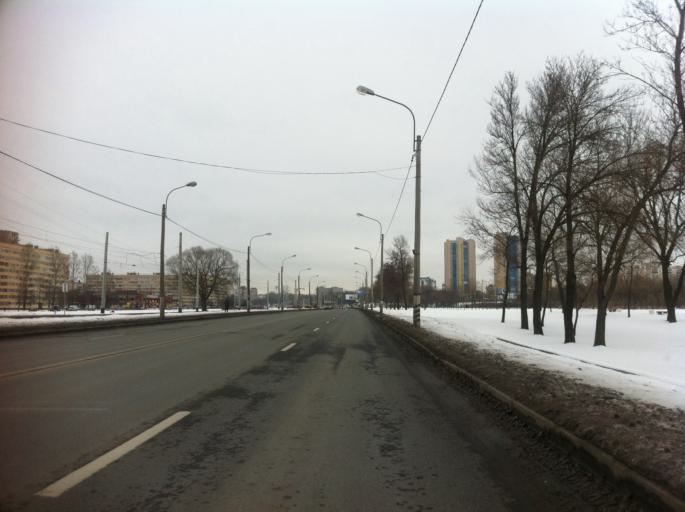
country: RU
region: St.-Petersburg
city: Uritsk
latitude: 59.8458
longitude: 30.1983
